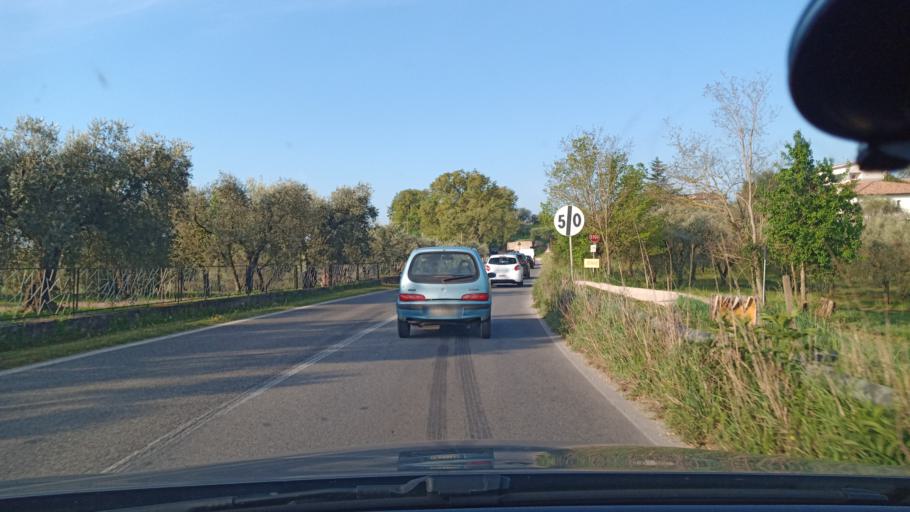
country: IT
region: Latium
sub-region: Citta metropolitana di Roma Capitale
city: Fiano Romano
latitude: 42.1858
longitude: 12.6386
